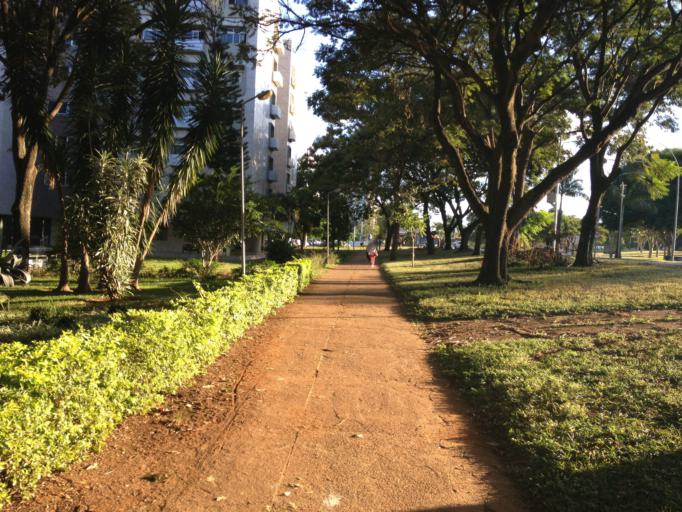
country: BR
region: Federal District
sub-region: Brasilia
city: Brasilia
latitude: -15.8054
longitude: -47.8877
